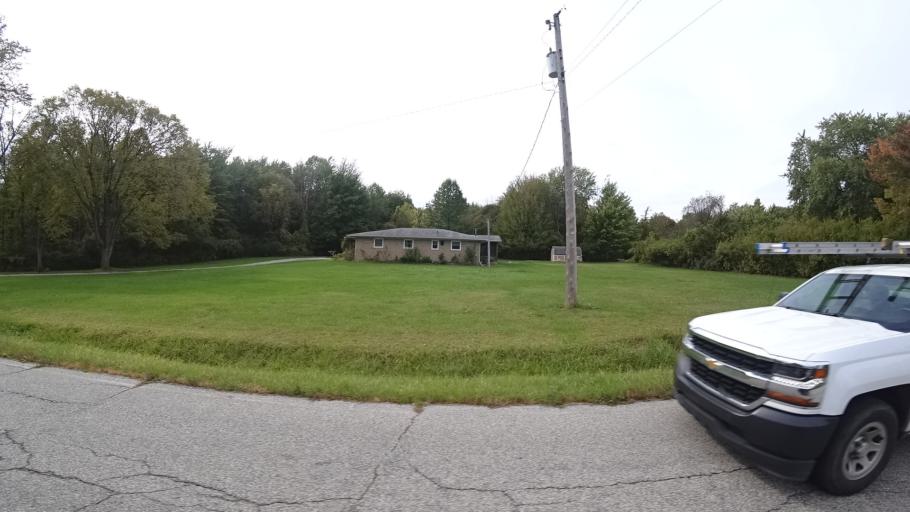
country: US
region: Indiana
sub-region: LaPorte County
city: Trail Creek
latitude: 41.6992
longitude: -86.8164
